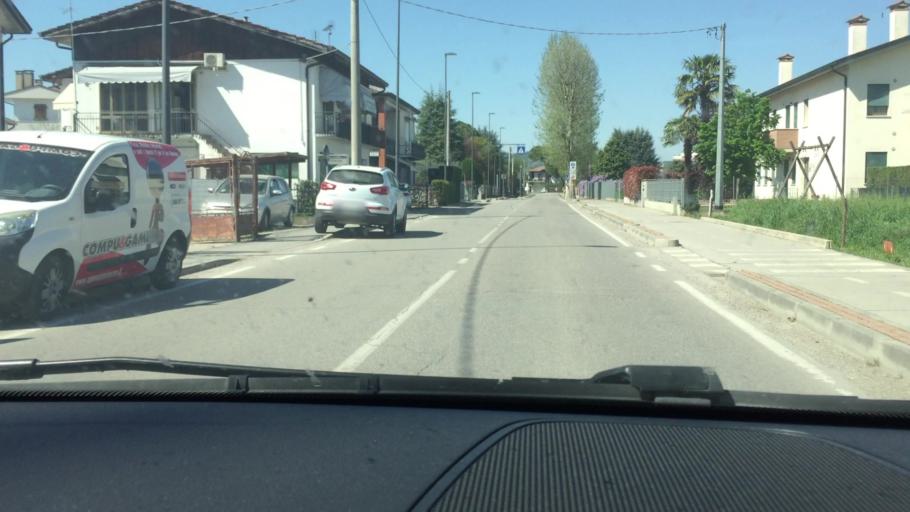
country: IT
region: Veneto
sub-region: Provincia di Padova
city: Pernumia
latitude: 45.2601
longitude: 11.7885
